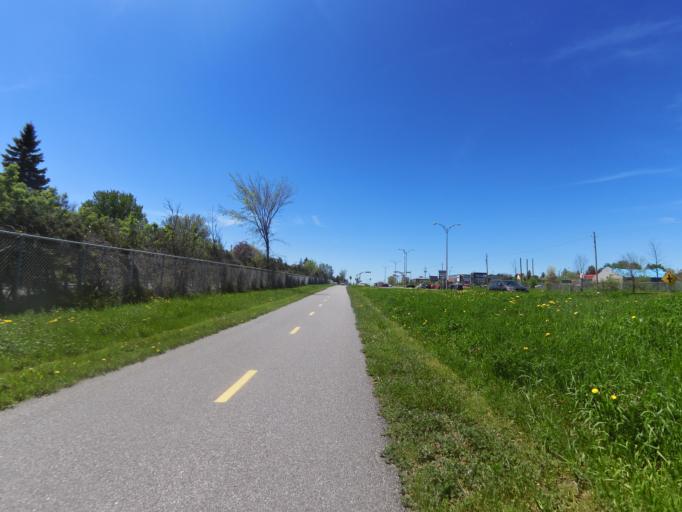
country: CA
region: Ontario
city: Bells Corners
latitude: 45.4104
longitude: -75.8370
